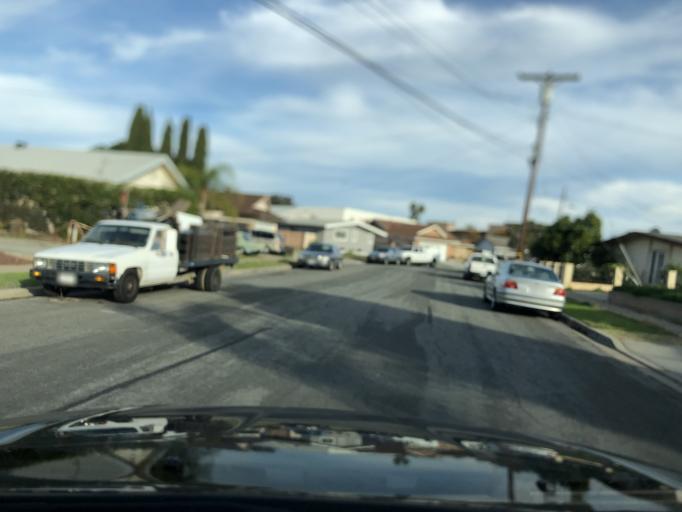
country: US
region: California
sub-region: San Diego County
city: La Jolla
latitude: 32.8281
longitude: -117.1742
